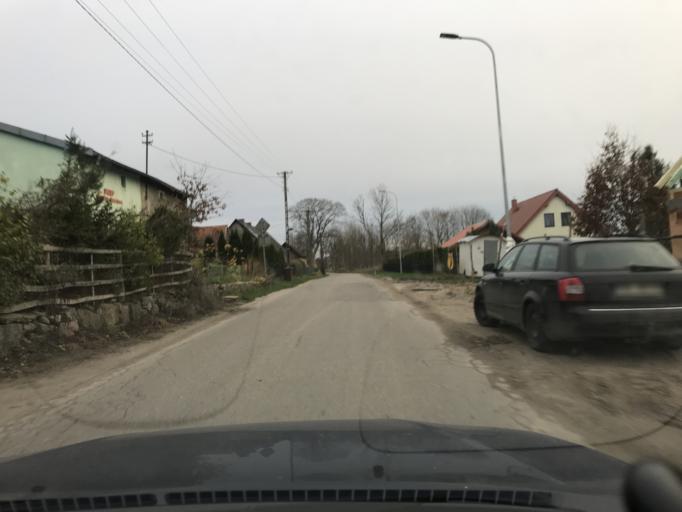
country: PL
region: Pomeranian Voivodeship
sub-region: Powiat slupski
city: Kobylnica
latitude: 54.4460
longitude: 16.8874
